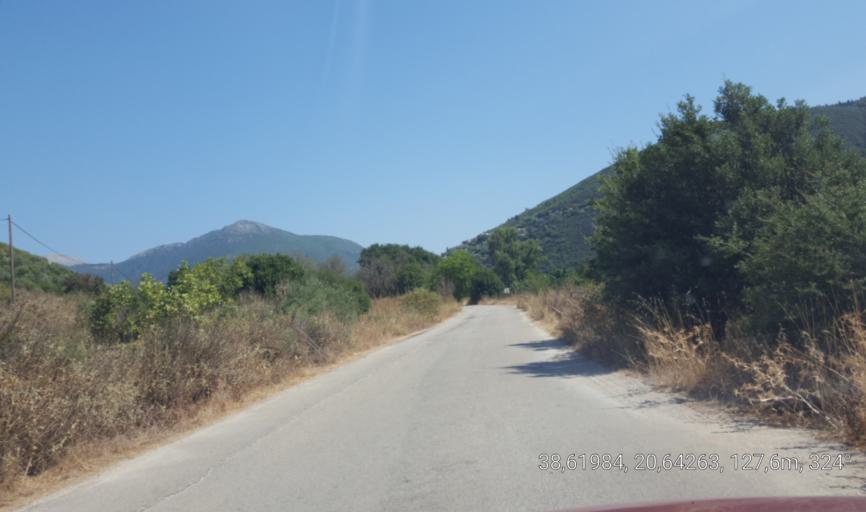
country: GR
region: Ionian Islands
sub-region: Lefkada
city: Nidri
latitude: 38.6197
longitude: 20.6425
